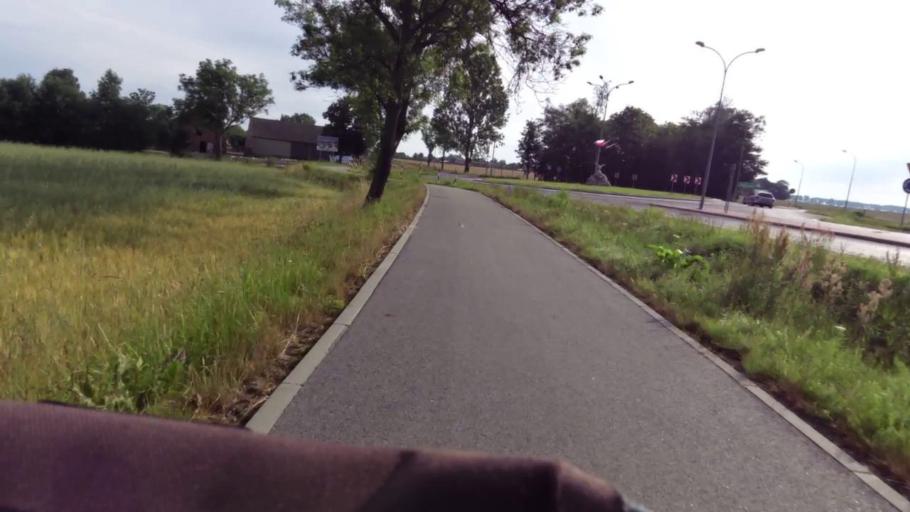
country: PL
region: West Pomeranian Voivodeship
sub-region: Powiat kamienski
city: Kamien Pomorski
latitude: 53.9931
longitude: 14.8154
